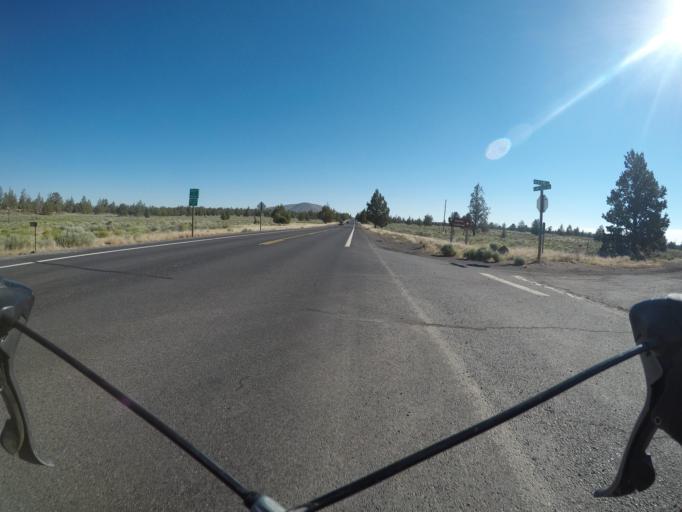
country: US
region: Oregon
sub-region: Deschutes County
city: Bend
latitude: 44.2106
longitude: -121.3180
